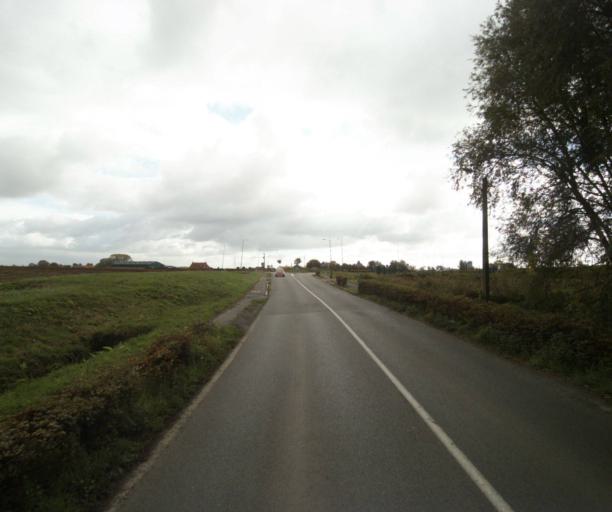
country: FR
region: Nord-Pas-de-Calais
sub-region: Departement du Nord
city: Quesnoy-sur-Deule
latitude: 50.6993
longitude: 3.0237
